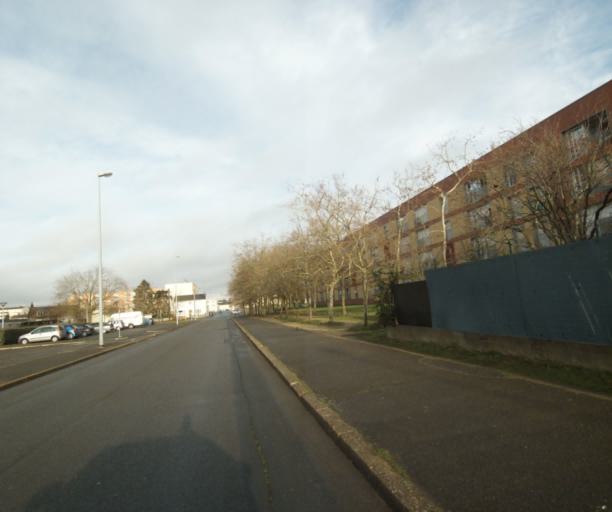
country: FR
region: Pays de la Loire
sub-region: Departement de la Sarthe
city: Le Mans
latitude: 47.9881
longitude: 0.2159
